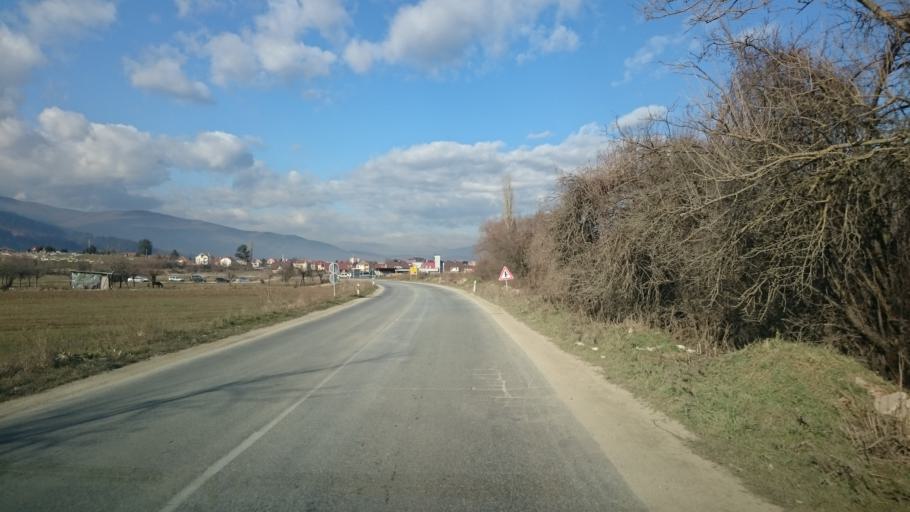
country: MK
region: Kicevo
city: Kicevo
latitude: 41.4964
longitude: 20.9624
